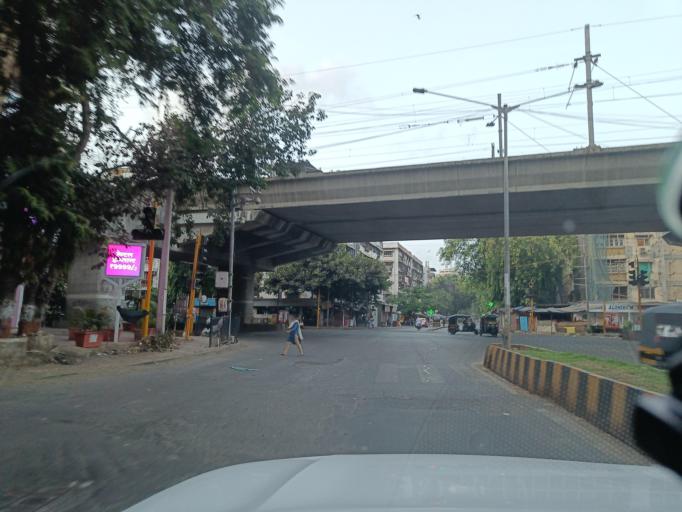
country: IN
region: Maharashtra
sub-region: Mumbai Suburban
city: Powai
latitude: 19.1297
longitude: 72.8257
